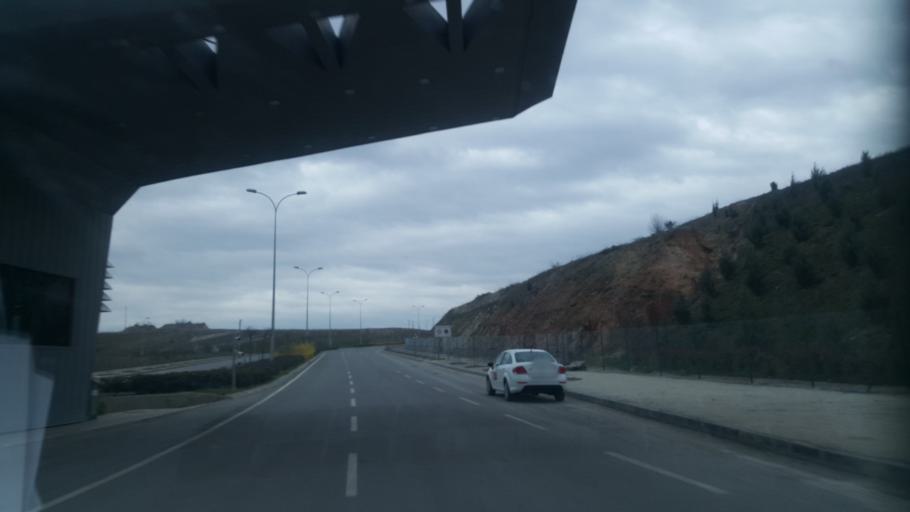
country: TR
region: Kocaeli
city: Tavsanli
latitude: 40.8277
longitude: 29.5615
